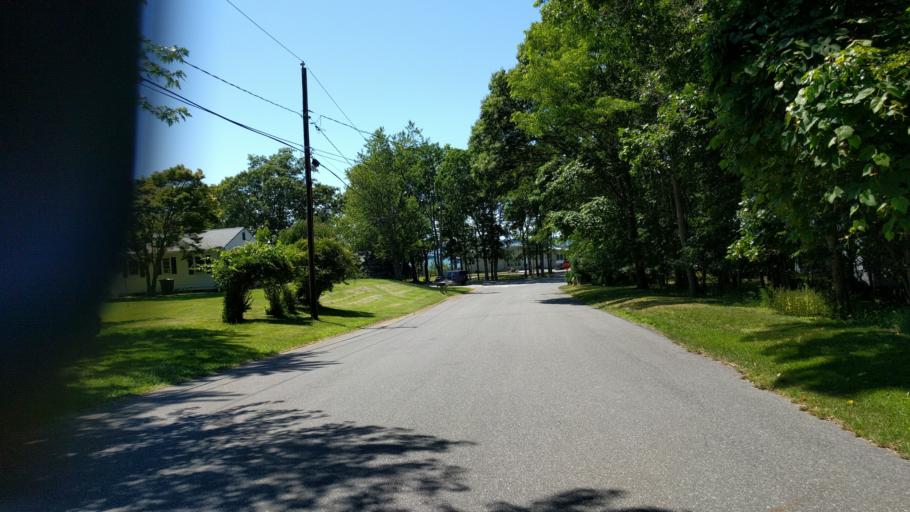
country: US
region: New York
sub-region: Suffolk County
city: Noyack
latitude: 40.9813
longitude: -72.3774
